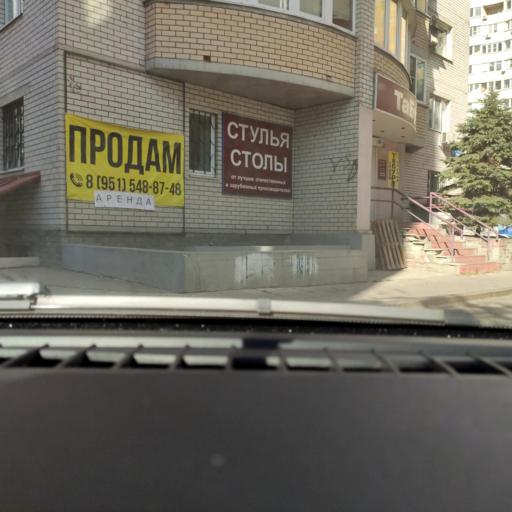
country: RU
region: Voronezj
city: Voronezh
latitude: 51.6464
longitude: 39.2345
